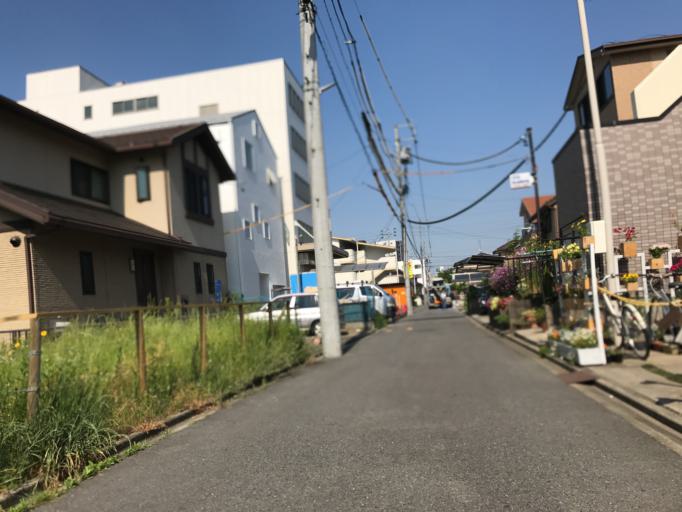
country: JP
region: Aichi
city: Nagoya-shi
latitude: 35.1762
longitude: 136.9280
